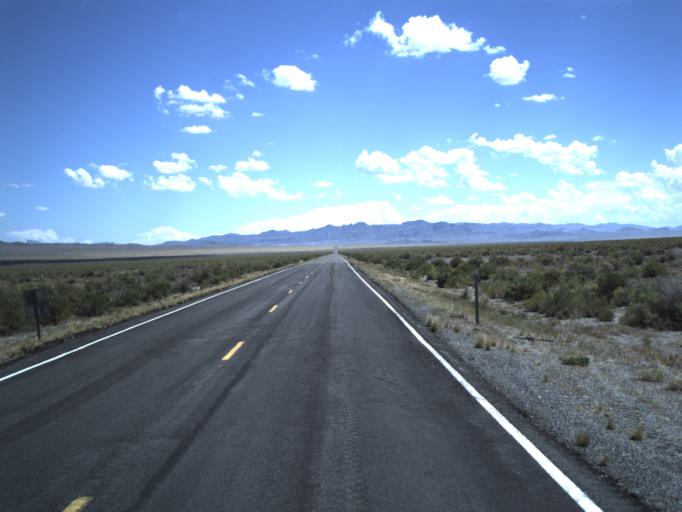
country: US
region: Nevada
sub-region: White Pine County
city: McGill
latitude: 39.0483
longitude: -113.9339
